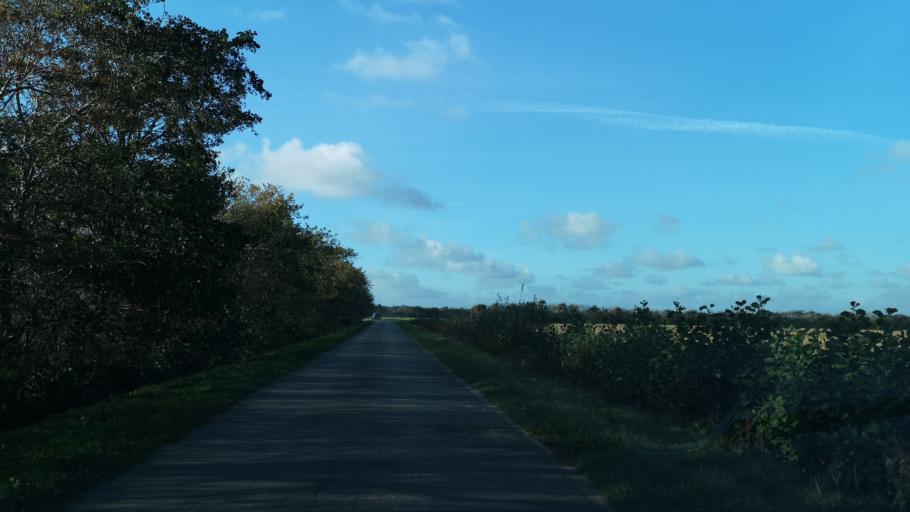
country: DK
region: Central Jutland
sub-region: Ringkobing-Skjern Kommune
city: Skjern
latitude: 55.8626
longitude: 8.3395
